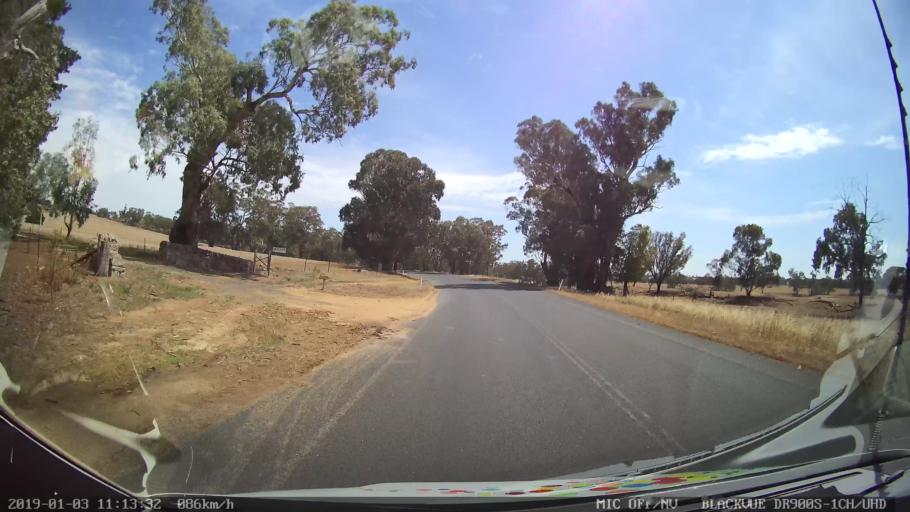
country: AU
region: New South Wales
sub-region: Young
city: Young
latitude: -34.1873
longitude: 148.2606
